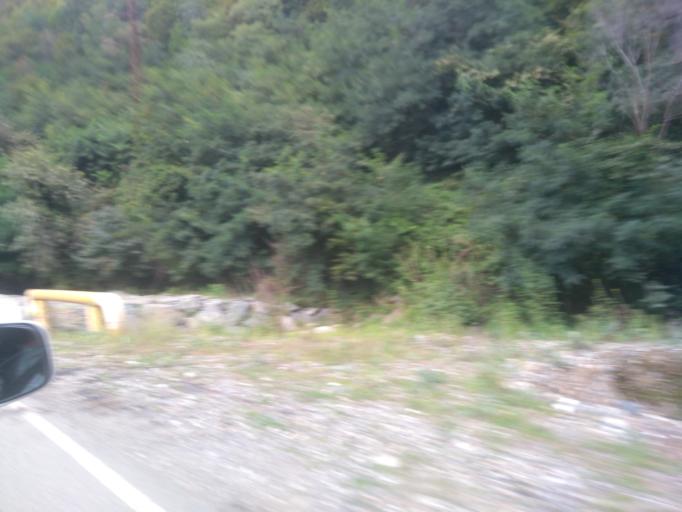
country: GE
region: Ajaria
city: Khelvachauri
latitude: 41.5492
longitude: 41.7054
